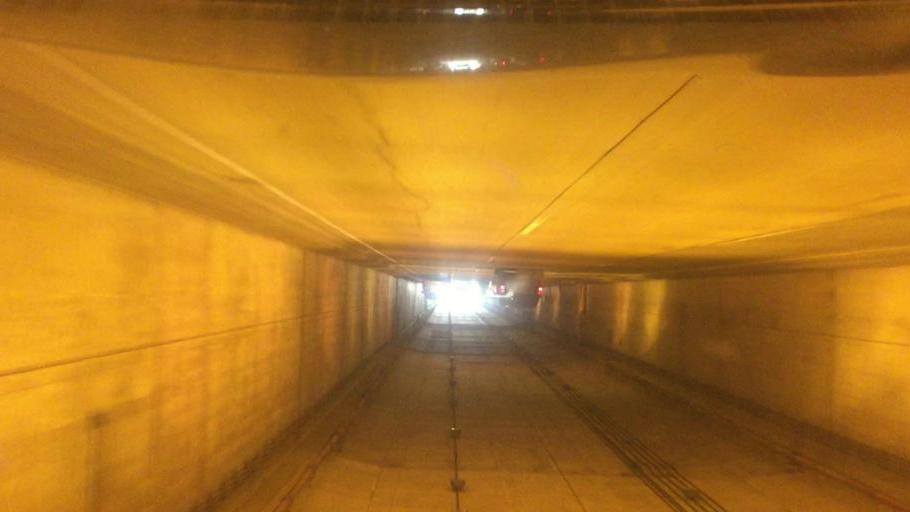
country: US
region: Michigan
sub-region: Wayne County
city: Romulus
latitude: 42.2013
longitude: -83.3590
